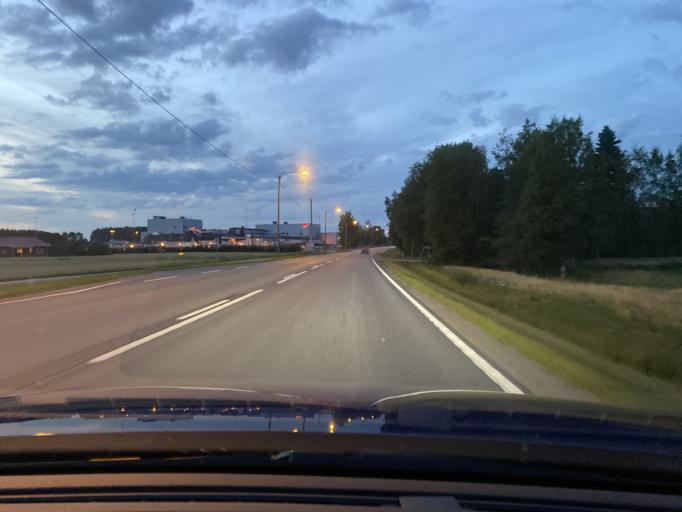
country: FI
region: Southern Ostrobothnia
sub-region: Suupohja
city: Kauhajoki
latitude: 62.4428
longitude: 22.2104
